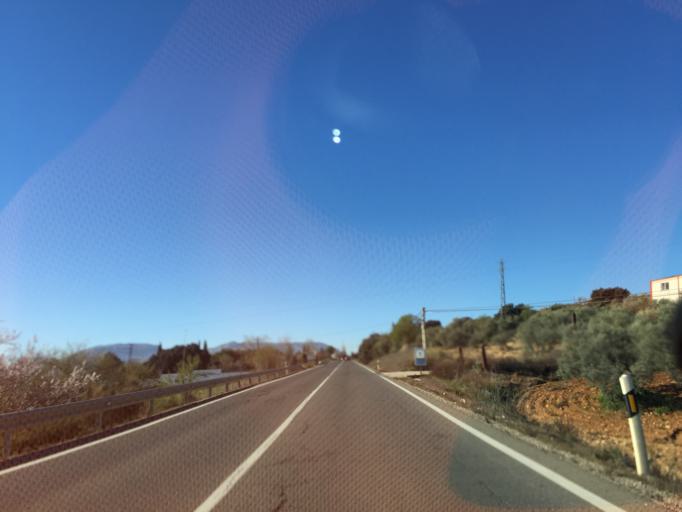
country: ES
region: Andalusia
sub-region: Provincia de Malaga
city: Arriate
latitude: 36.7678
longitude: -5.1297
